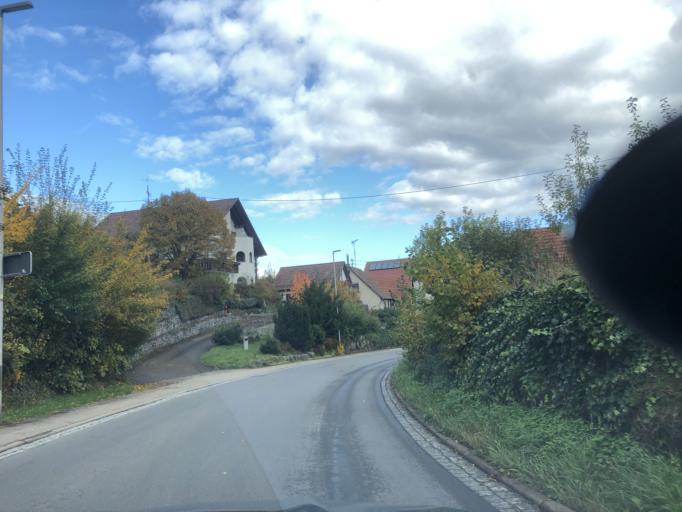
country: DE
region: Baden-Wuerttemberg
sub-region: Regierungsbezirk Stuttgart
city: Winterbach
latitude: 48.8400
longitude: 9.4520
